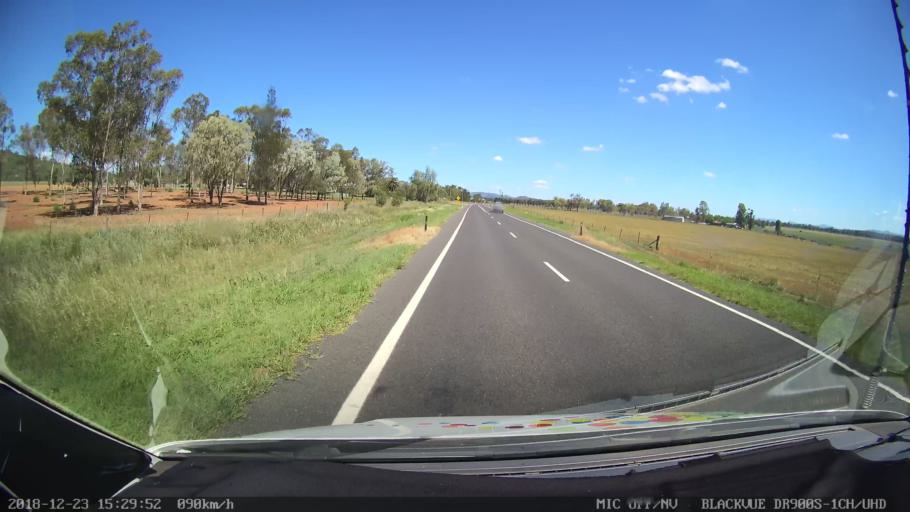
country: AU
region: New South Wales
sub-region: Tamworth Municipality
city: East Tamworth
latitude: -30.9516
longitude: 150.8642
